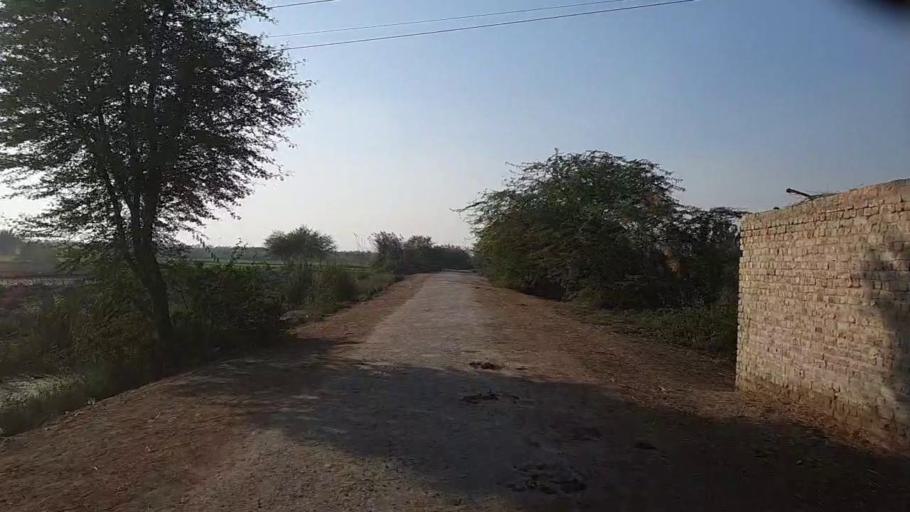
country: PK
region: Sindh
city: Ranipur
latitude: 27.2440
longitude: 68.5062
